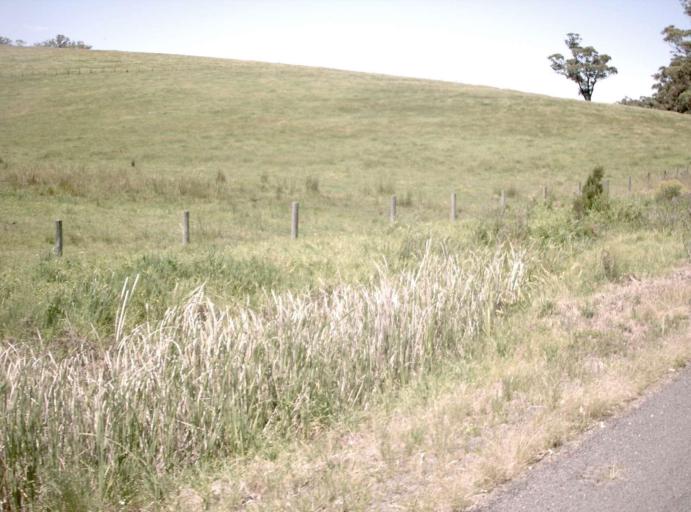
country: AU
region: Victoria
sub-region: East Gippsland
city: Lakes Entrance
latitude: -37.7051
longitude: 148.5408
